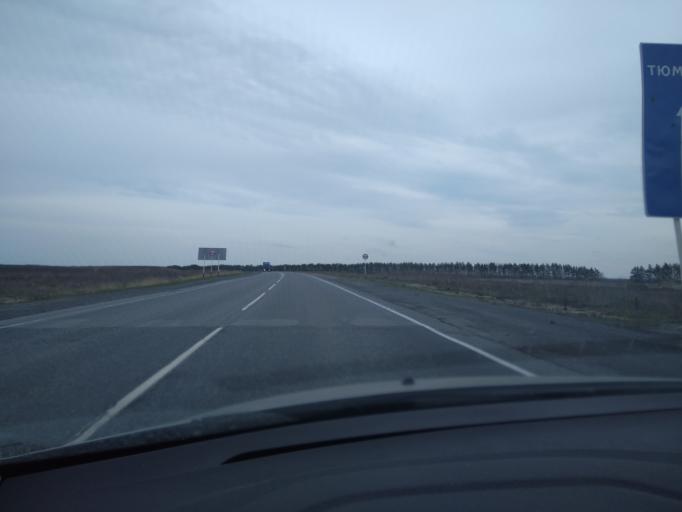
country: RU
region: Sverdlovsk
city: Kamyshlov
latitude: 56.8490
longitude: 62.8266
